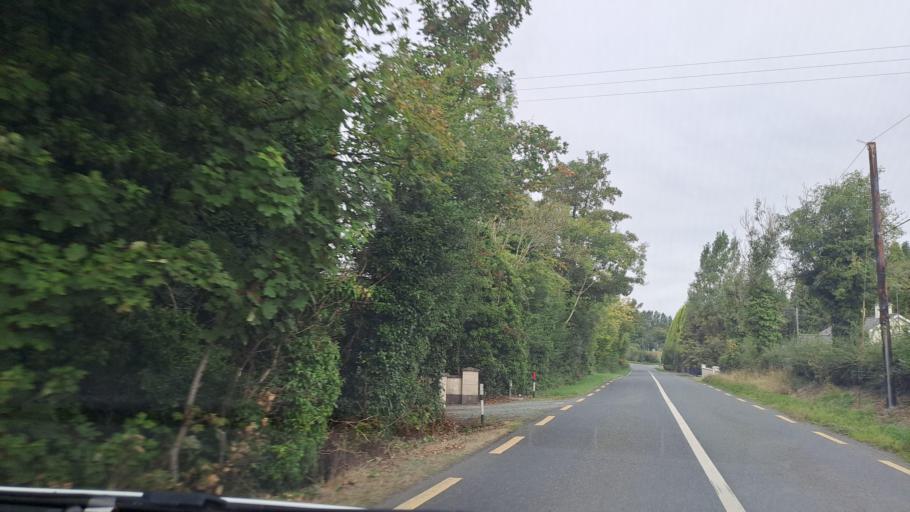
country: IE
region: Ulster
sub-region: An Cabhan
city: Kingscourt
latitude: 53.8968
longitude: -6.7668
